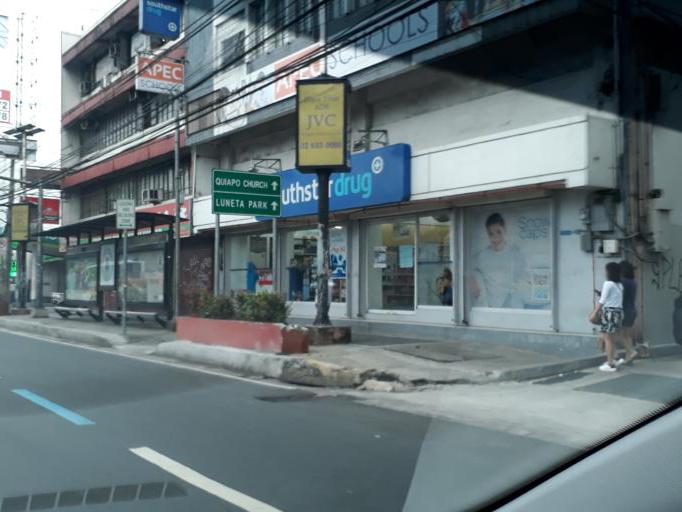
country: PH
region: Metro Manila
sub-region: City of Manila
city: Manila
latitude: 14.6153
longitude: 120.9989
